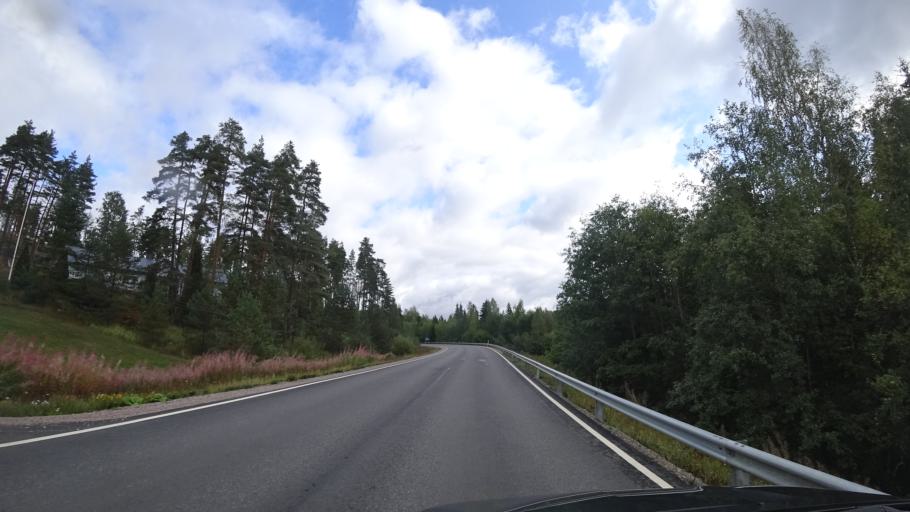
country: FI
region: Haeme
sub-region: Haemeenlinna
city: Lammi
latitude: 60.9434
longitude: 25.0150
